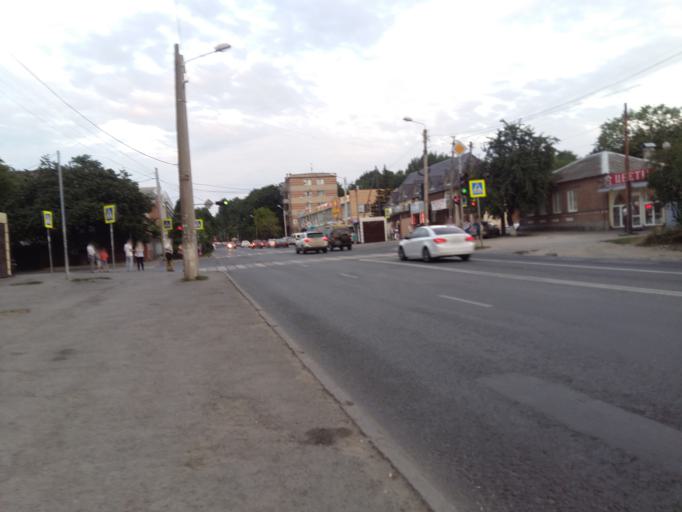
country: RU
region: Rostov
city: Imeni Chkalova
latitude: 47.2748
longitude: 39.7405
